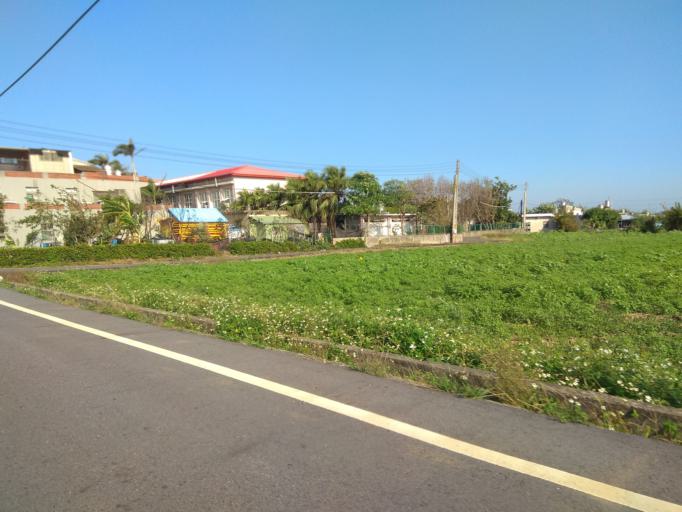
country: TW
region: Taiwan
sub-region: Hsinchu
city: Zhubei
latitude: 25.0040
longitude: 121.0502
